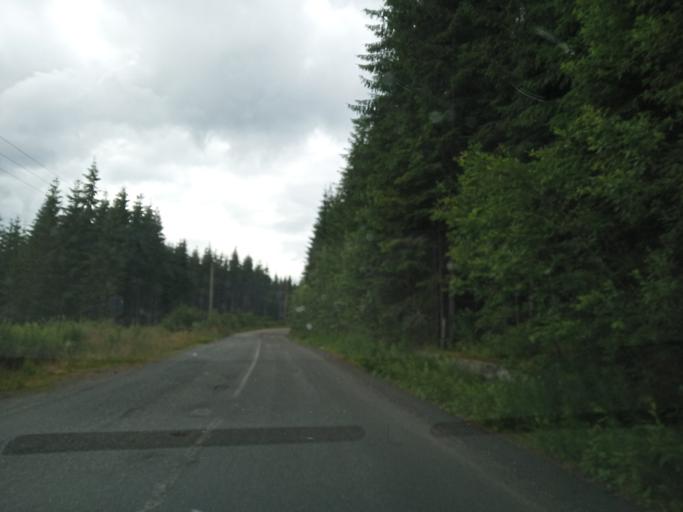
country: RO
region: Gorj
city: Novaci-Straini
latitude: 45.4196
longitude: 23.7012
